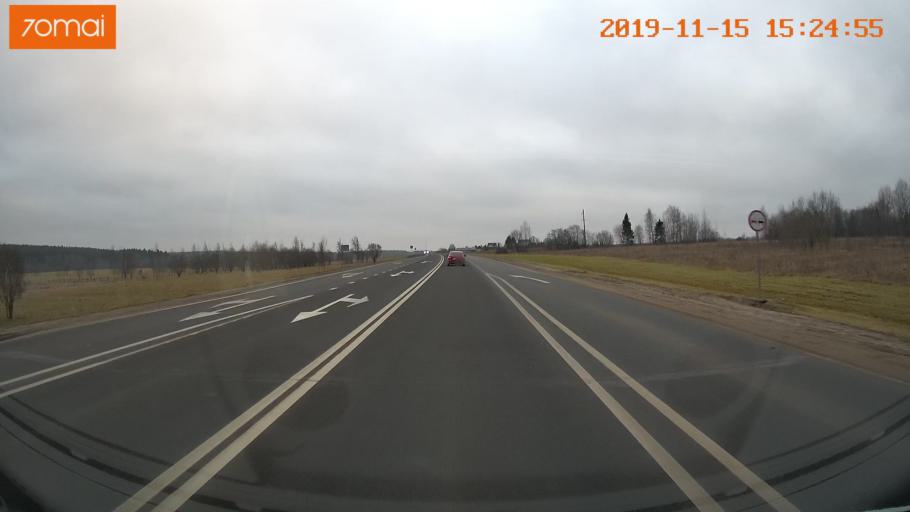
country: RU
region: Jaroslavl
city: Danilov
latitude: 58.1713
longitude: 40.1342
